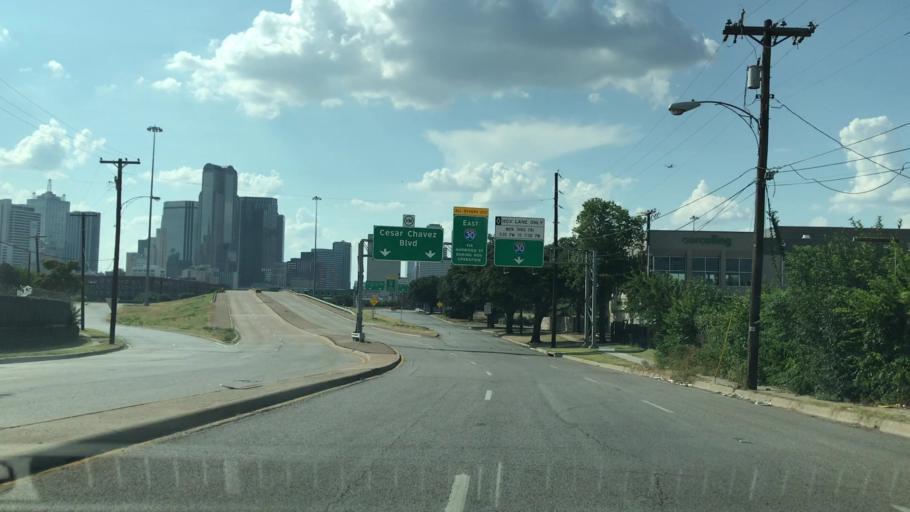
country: US
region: Texas
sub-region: Dallas County
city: Dallas
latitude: 32.7735
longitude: -96.7831
